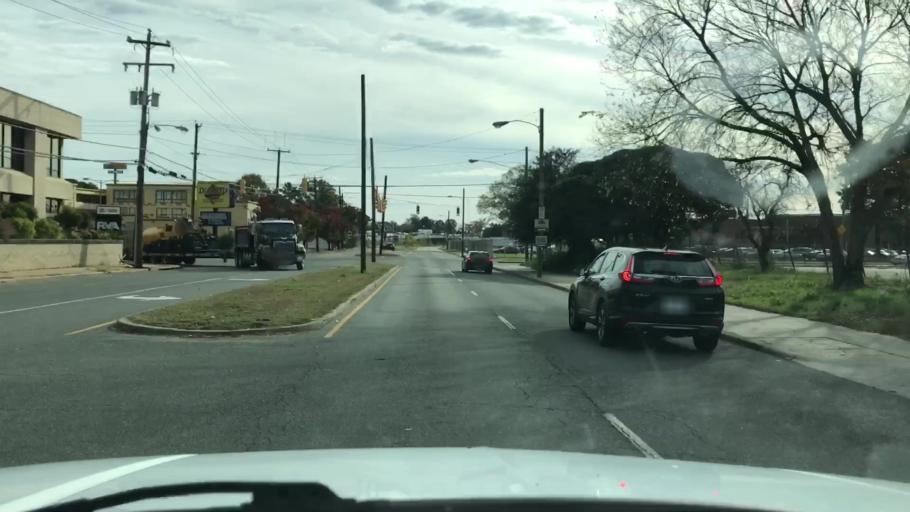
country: US
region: Virginia
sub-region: City of Richmond
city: Richmond
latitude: 37.5735
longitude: -77.4619
